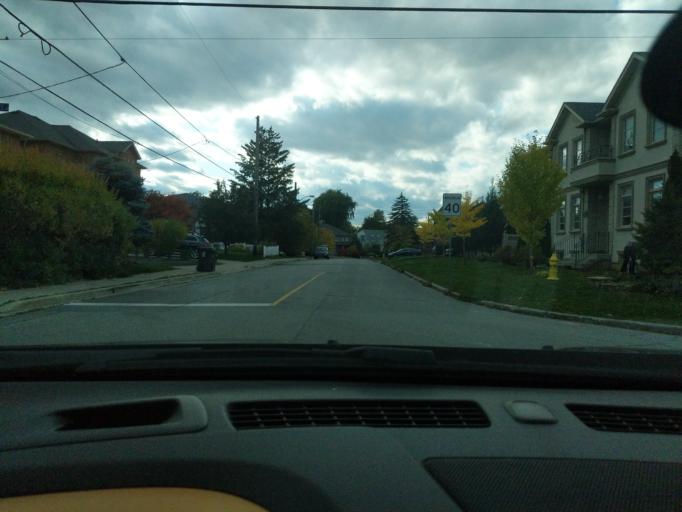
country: CA
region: Ontario
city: Toronto
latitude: 43.7200
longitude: -79.4347
